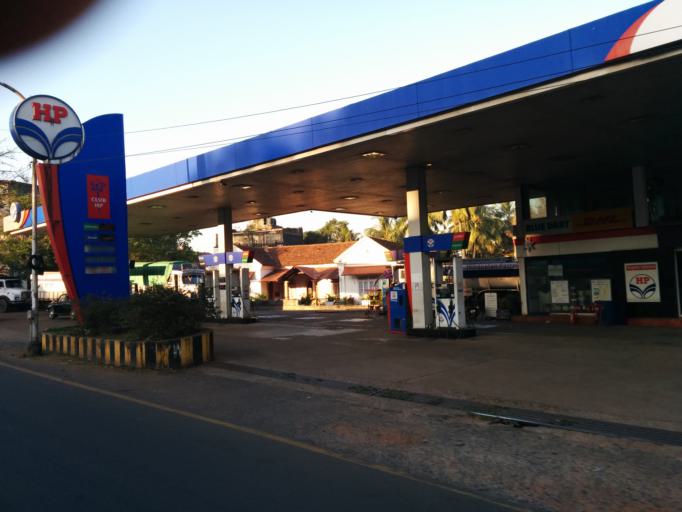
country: IN
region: Goa
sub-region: South Goa
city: Madgaon
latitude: 15.2771
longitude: 73.9586
